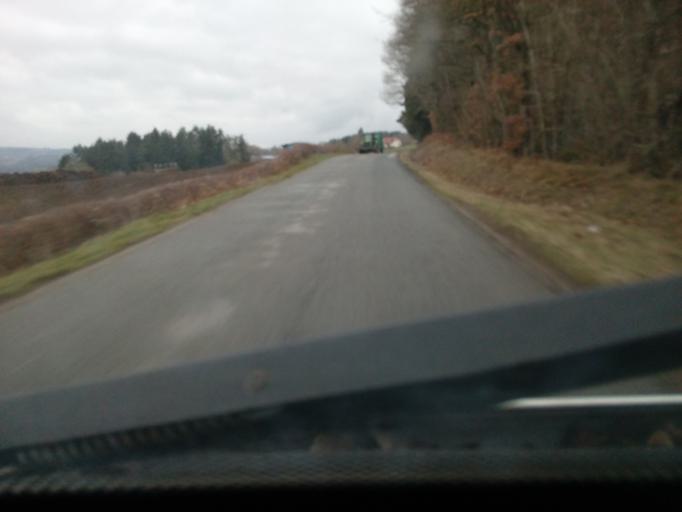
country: FR
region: Limousin
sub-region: Departement de la Creuse
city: Felletin
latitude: 45.8729
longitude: 2.2020
